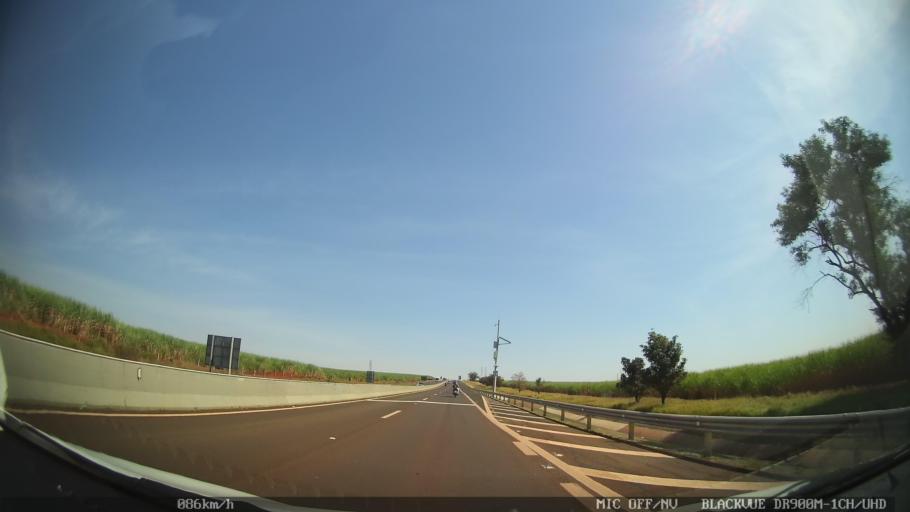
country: BR
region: Sao Paulo
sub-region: Ribeirao Preto
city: Ribeirao Preto
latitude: -21.1659
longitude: -47.8815
